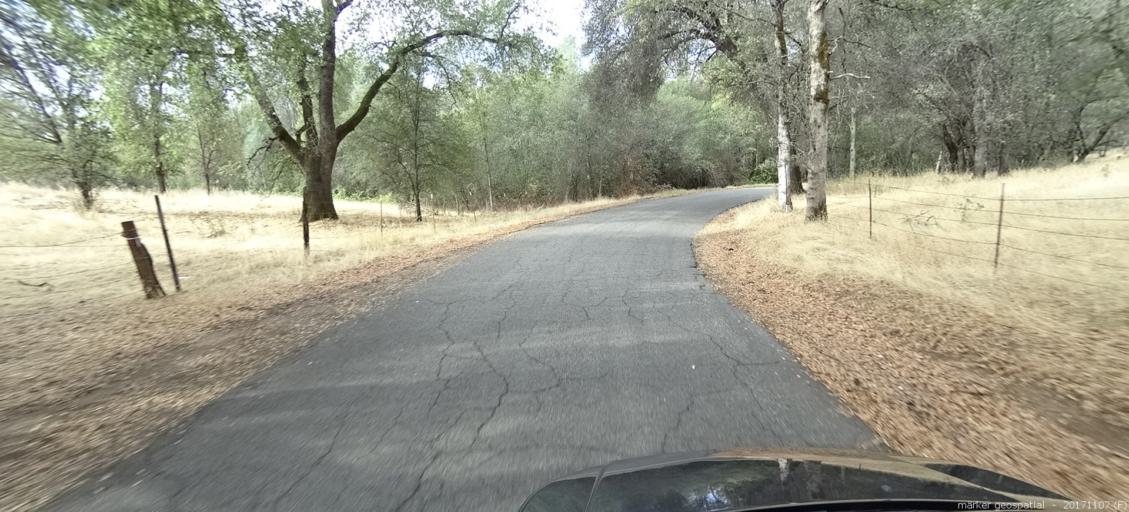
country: US
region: California
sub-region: Shasta County
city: Shasta
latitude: 40.5014
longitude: -122.5875
